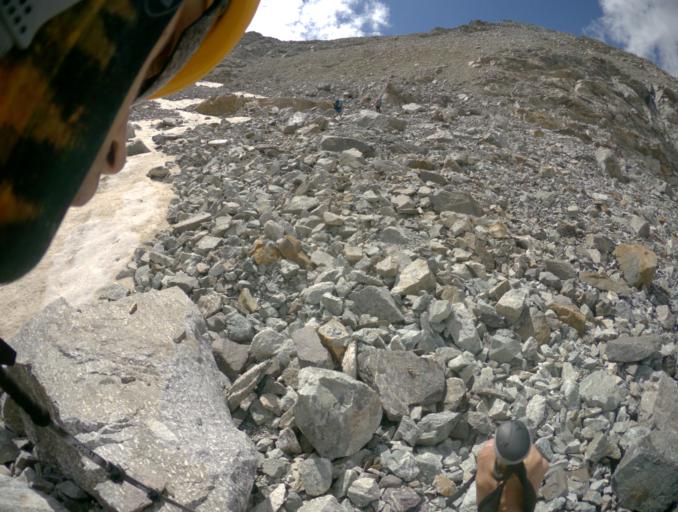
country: RU
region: Karachayevo-Cherkesiya
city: Uchkulan
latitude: 43.3189
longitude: 42.0794
